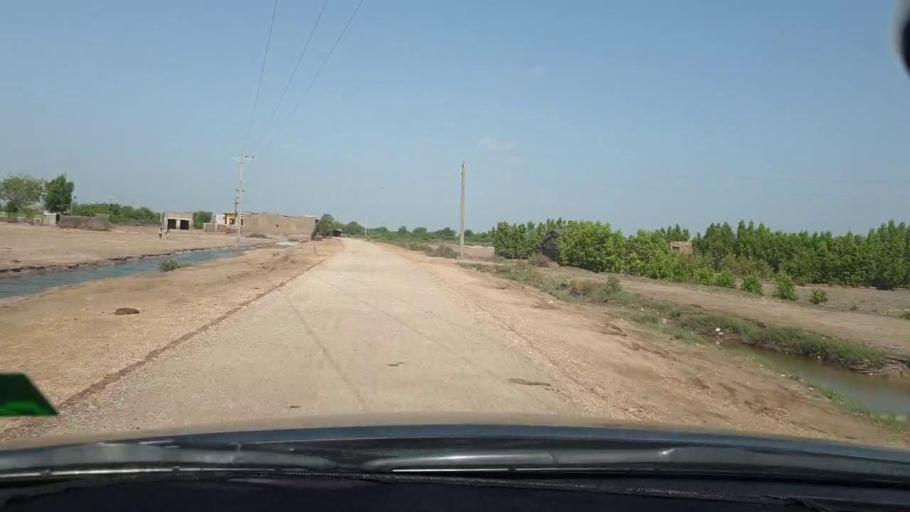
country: PK
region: Sindh
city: Tando Bago
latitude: 24.8968
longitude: 69.0993
